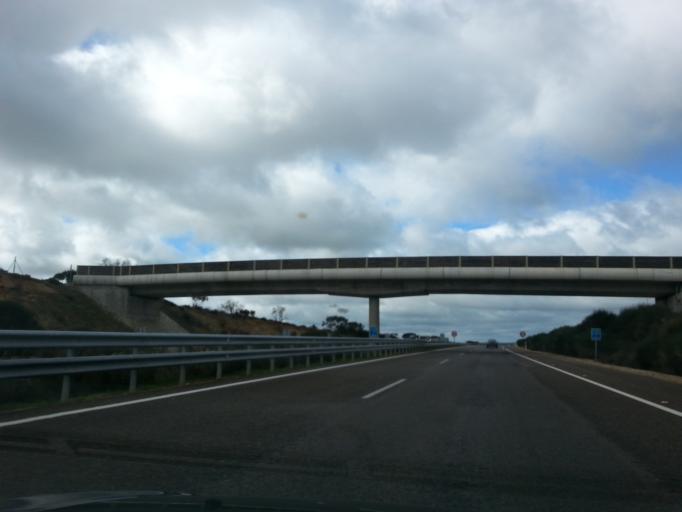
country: ES
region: Castille and Leon
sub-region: Provincia de Salamanca
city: San Munoz
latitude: 40.8170
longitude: -6.1260
